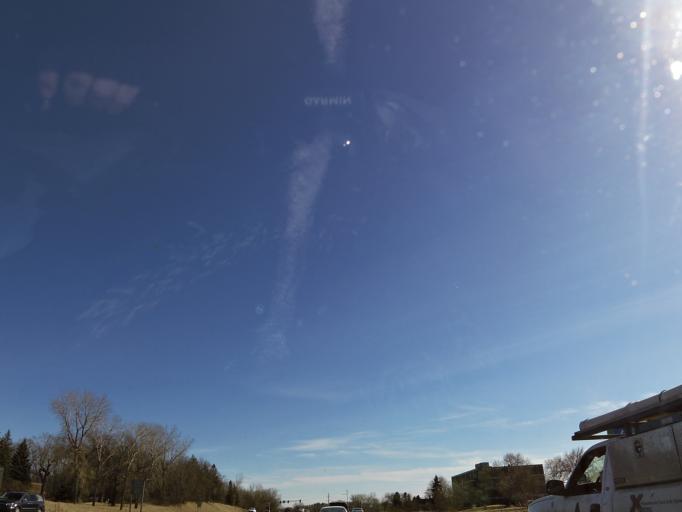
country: US
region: Minnesota
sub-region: Hennepin County
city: Plymouth
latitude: 45.0018
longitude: -93.4437
